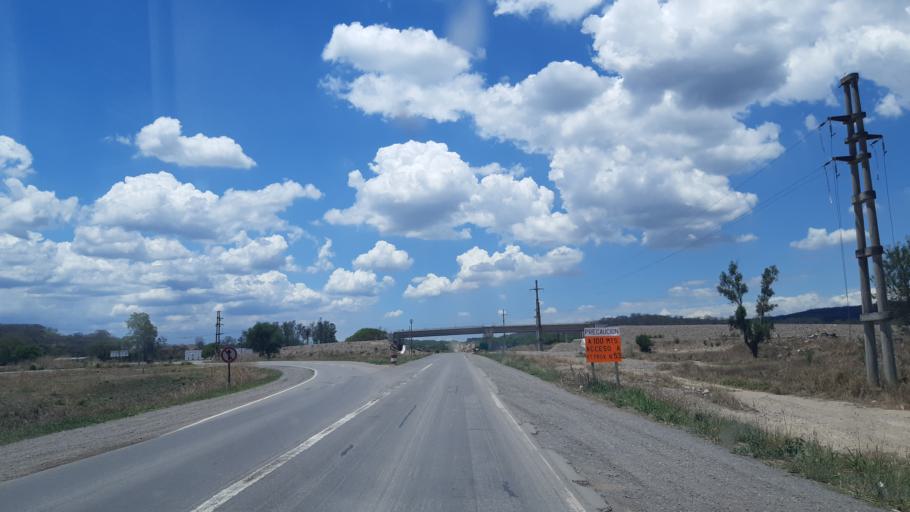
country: AR
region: Jujuy
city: La Mendieta
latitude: -24.4362
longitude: -65.0106
